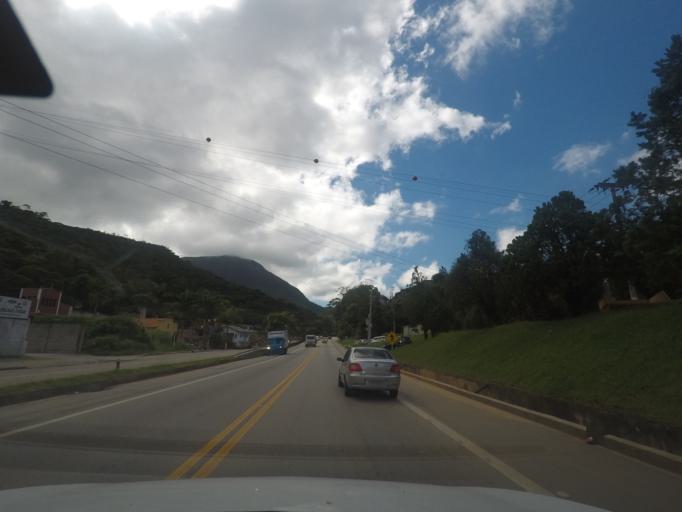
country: BR
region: Rio de Janeiro
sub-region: Teresopolis
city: Teresopolis
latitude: -22.4004
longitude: -42.9543
